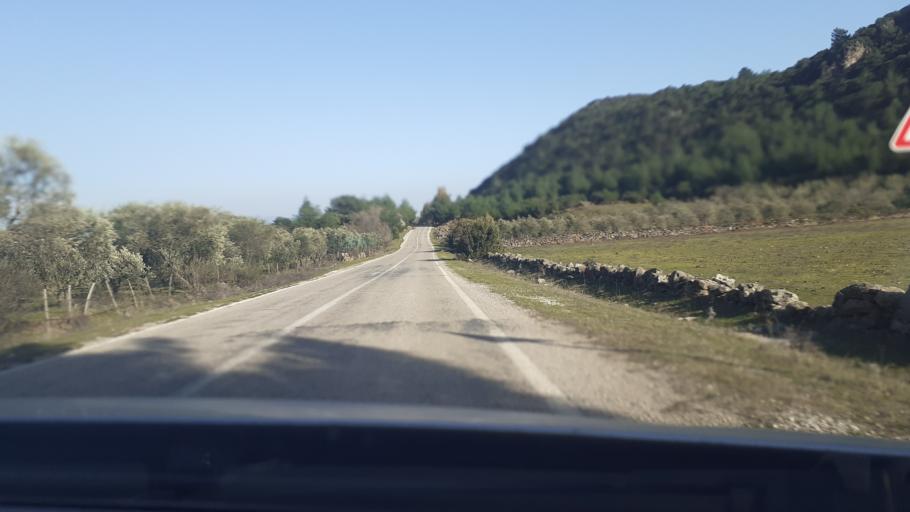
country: TR
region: Hatay
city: Aktepe
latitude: 36.7335
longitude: 36.4701
